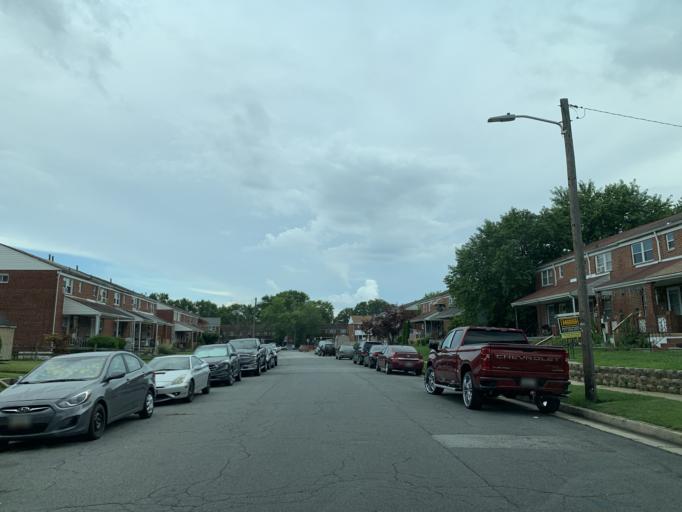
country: US
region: Maryland
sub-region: Baltimore County
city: Essex
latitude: 39.2960
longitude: -76.4526
